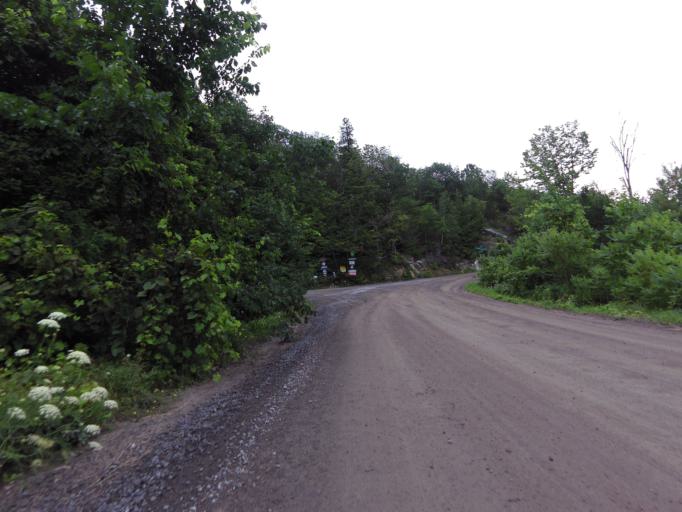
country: CA
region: Ontario
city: Kingston
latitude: 44.5540
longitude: -76.6096
